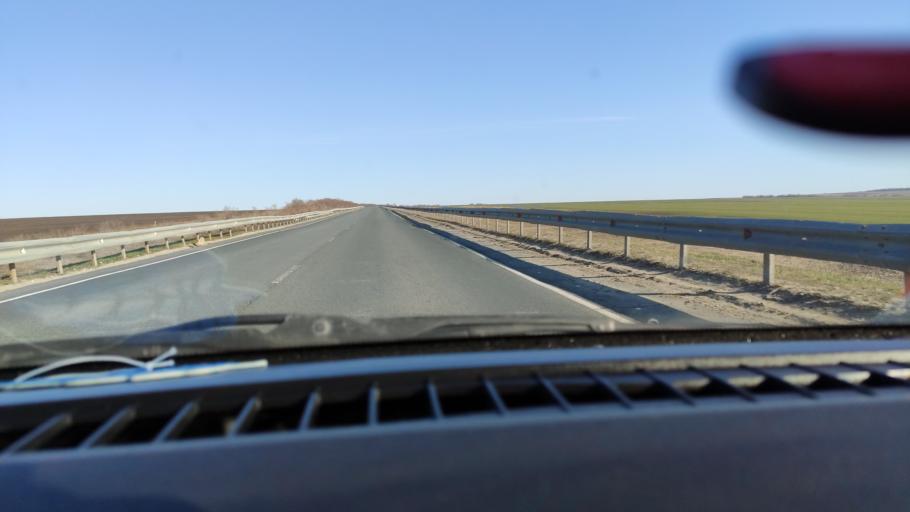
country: RU
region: Saratov
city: Dukhovnitskoye
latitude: 52.7553
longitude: 48.2450
